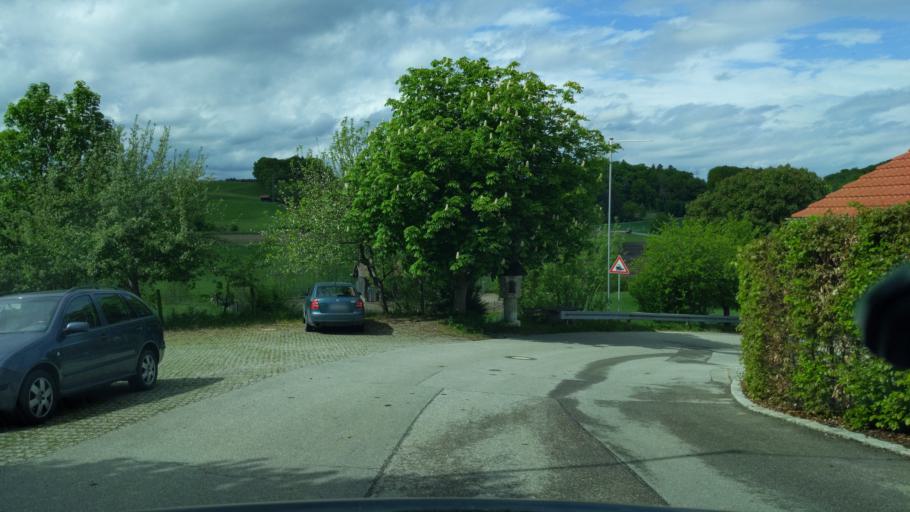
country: DE
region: Bavaria
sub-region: Upper Bavaria
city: Ebersberg
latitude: 48.0793
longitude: 11.9963
